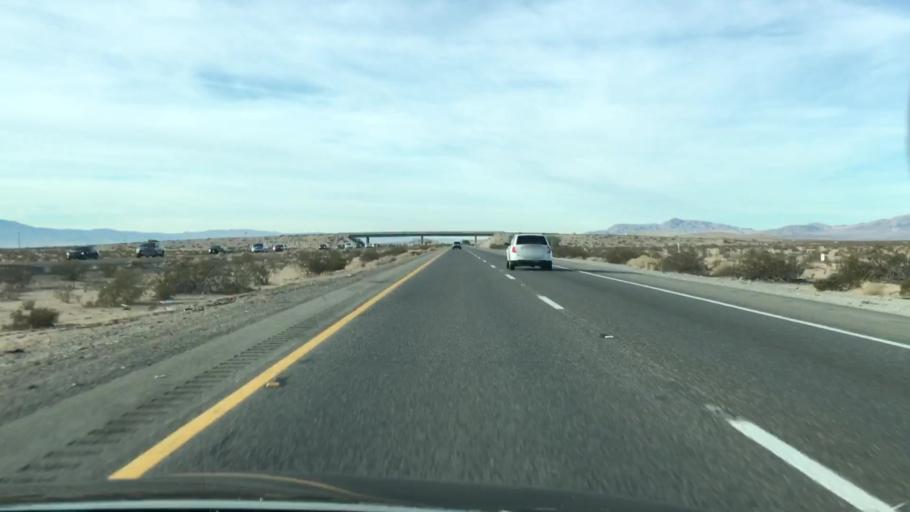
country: US
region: California
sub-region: San Bernardino County
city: Fort Irwin
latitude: 34.9866
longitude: -116.5926
